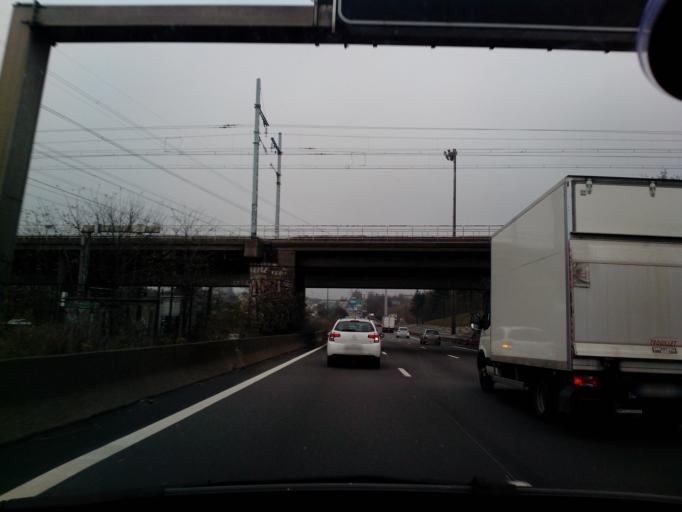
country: FR
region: Ile-de-France
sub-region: Departement de l'Essonne
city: Wissous
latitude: 48.7437
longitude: 2.3234
